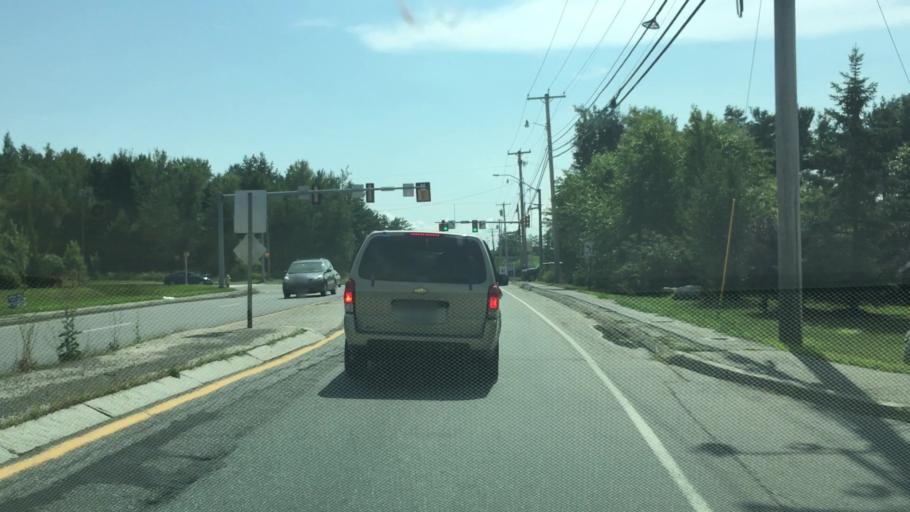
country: US
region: Maine
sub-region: Penobscot County
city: Brewer
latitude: 44.8265
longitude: -68.7569
